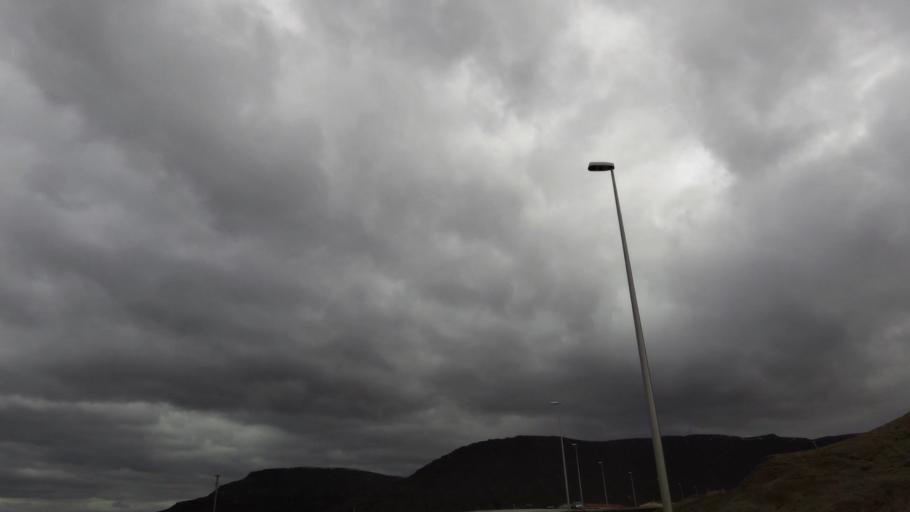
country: IS
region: Westfjords
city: Isafjoerdur
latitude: 66.1074
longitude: -23.1112
